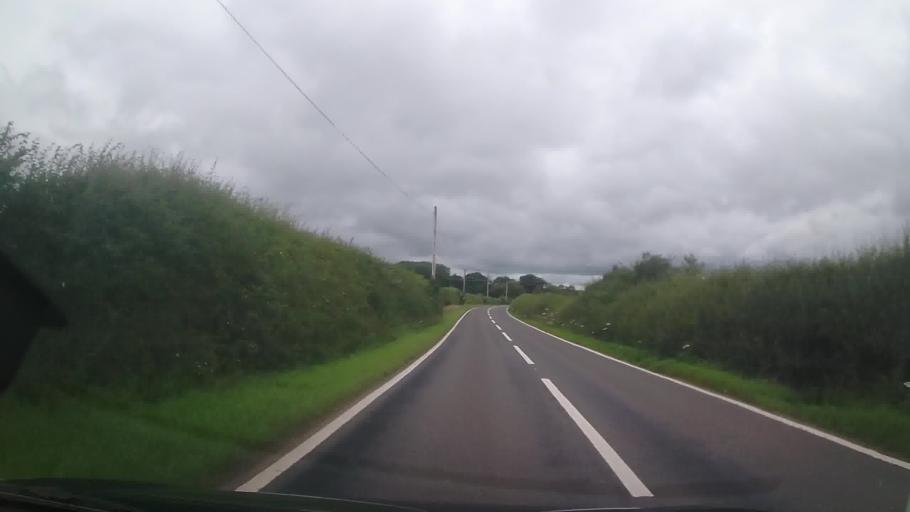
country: GB
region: England
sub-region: Shropshire
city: Petton
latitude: 52.8210
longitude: -2.7969
